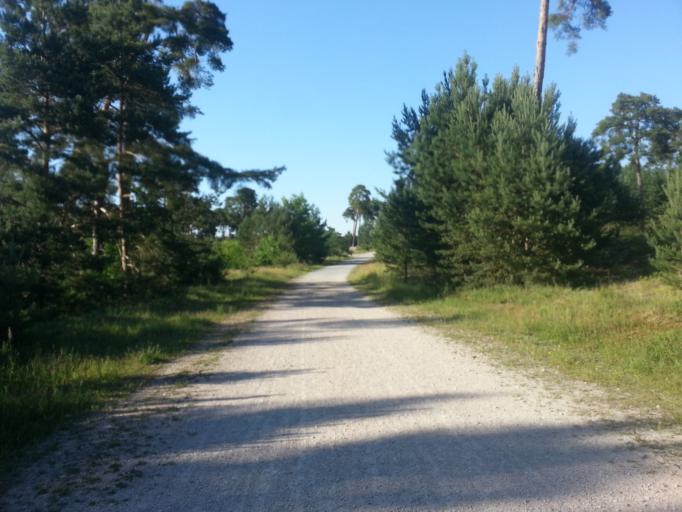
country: DE
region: Hesse
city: Viernheim
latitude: 49.5378
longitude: 8.5460
